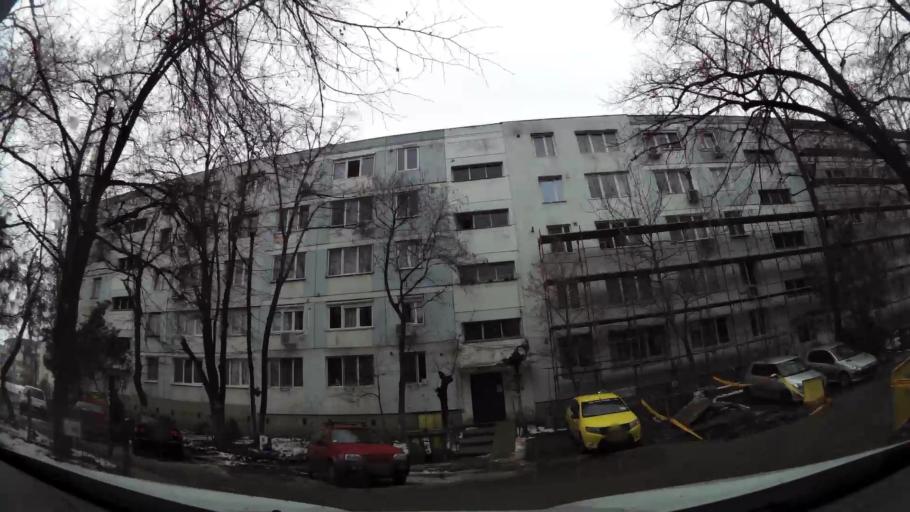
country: RO
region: Ilfov
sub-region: Comuna Chiajna
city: Rosu
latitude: 44.4217
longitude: 26.0134
